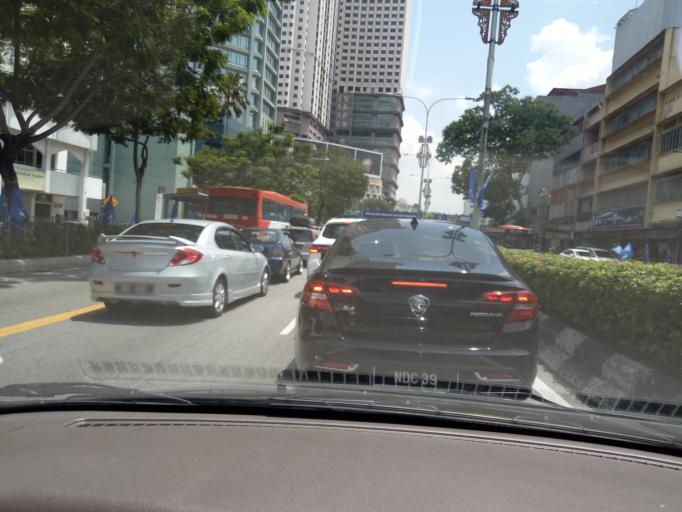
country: MY
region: Kuala Lumpur
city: Kuala Lumpur
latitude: 3.1709
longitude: 101.6937
